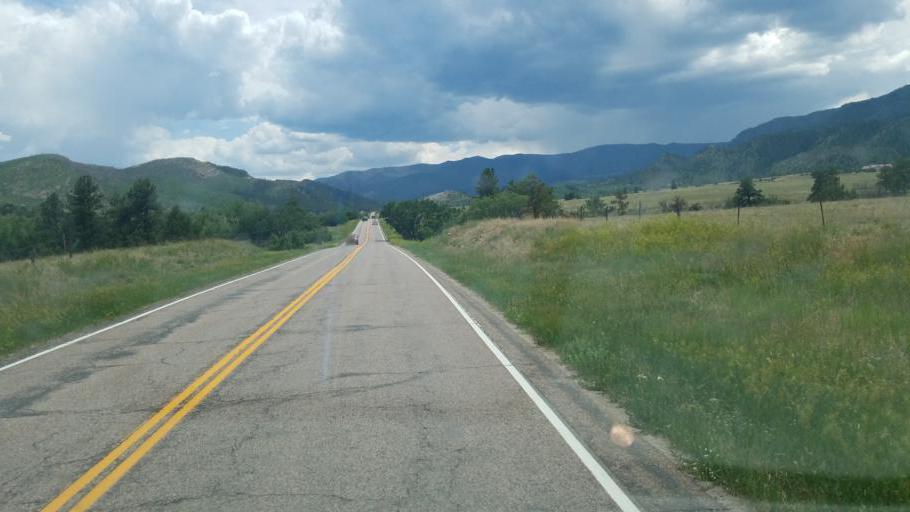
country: US
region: Colorado
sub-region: Fremont County
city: Florence
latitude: 38.2297
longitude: -105.0910
